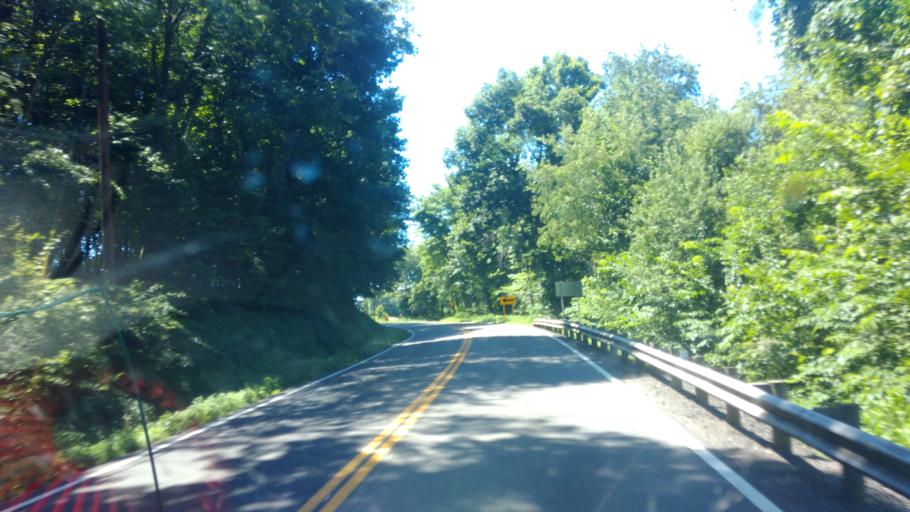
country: US
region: Ohio
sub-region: Carroll County
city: Carrollton
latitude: 40.4868
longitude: -80.9422
